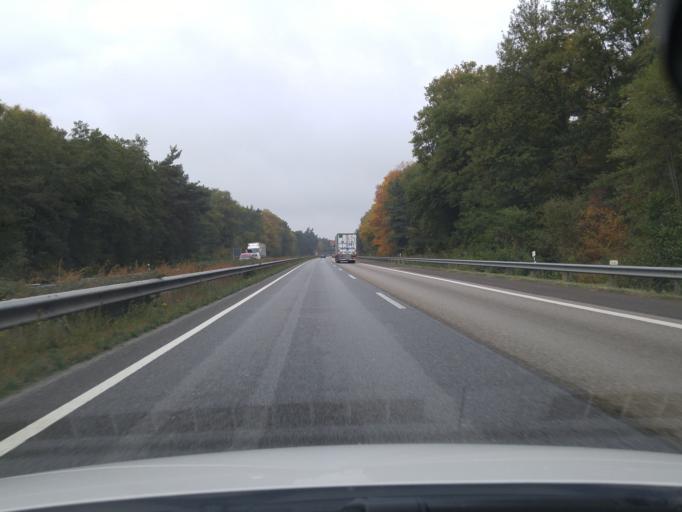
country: DE
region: Rheinland-Pfalz
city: Schifferstadt
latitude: 49.3604
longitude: 8.3664
